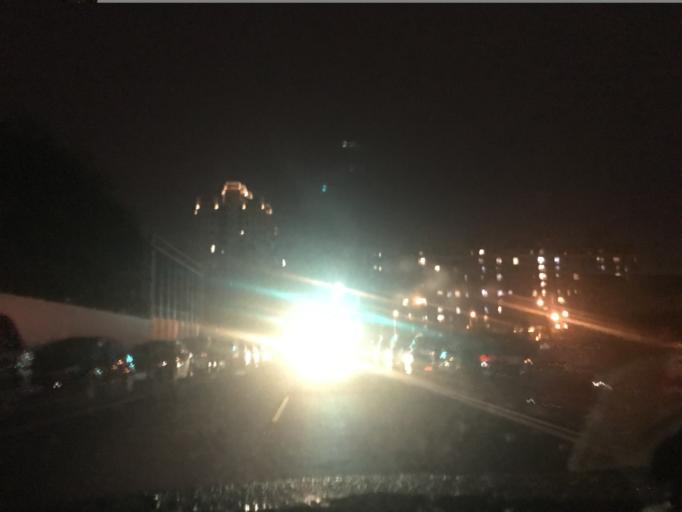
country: TW
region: Taiwan
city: Daxi
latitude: 24.9331
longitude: 121.2822
